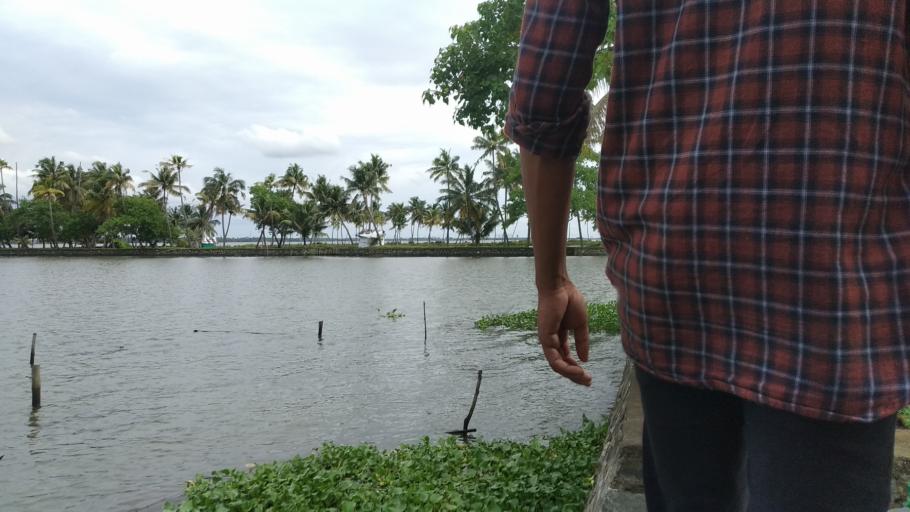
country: IN
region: Kerala
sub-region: Ernakulam
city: Elur
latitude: 10.0818
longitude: 76.2243
